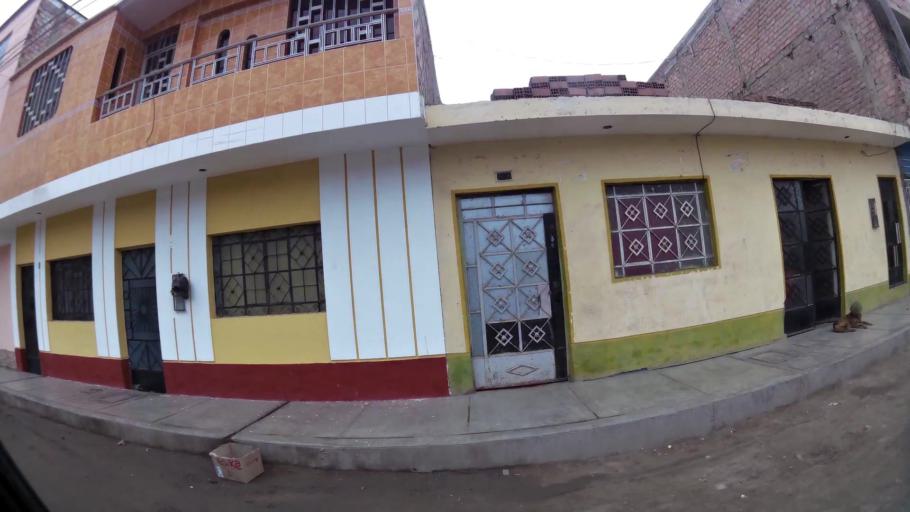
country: PE
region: Lima
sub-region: Barranca
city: Barranca
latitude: -10.7463
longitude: -77.7537
